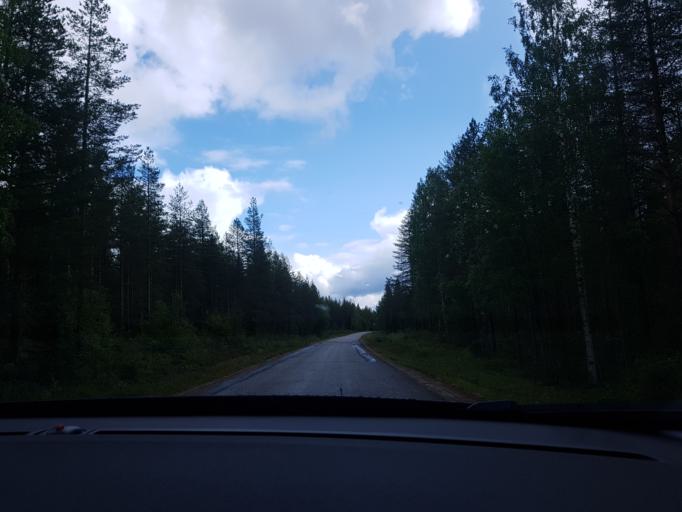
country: FI
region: Kainuu
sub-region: Kehys-Kainuu
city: Kuhmo
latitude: 64.4606
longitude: 29.6237
